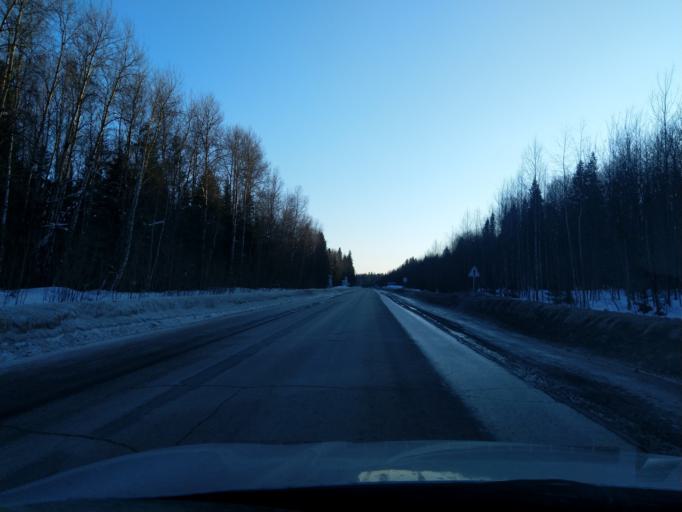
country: RU
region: Perm
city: Dobryanka
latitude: 58.4495
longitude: 56.5446
